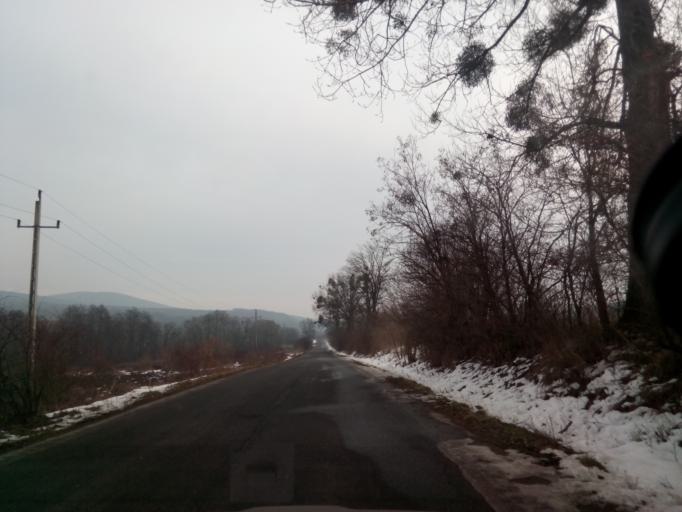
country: HU
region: Borsod-Abauj-Zemplen
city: Gonc
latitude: 48.5066
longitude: 21.3207
